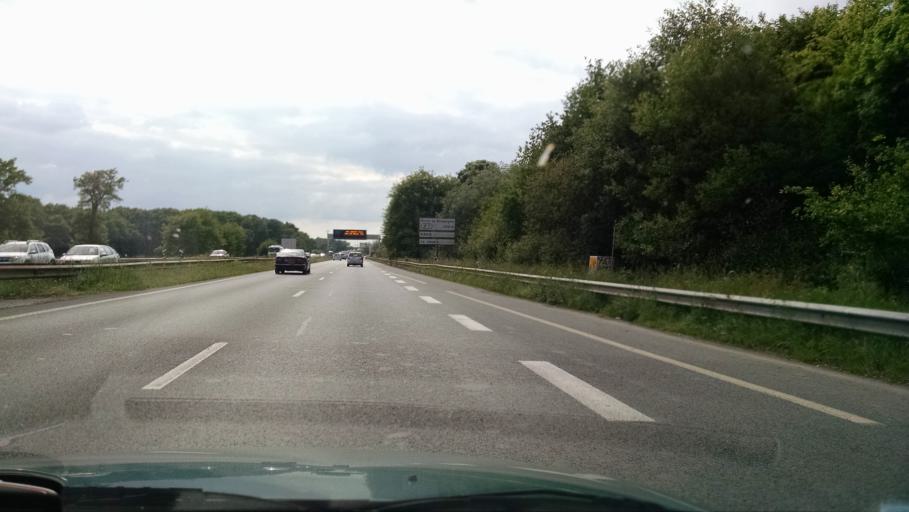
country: FR
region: Brittany
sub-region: Departement d'Ille-et-Vilaine
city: Rennes
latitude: 48.0800
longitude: -1.6826
